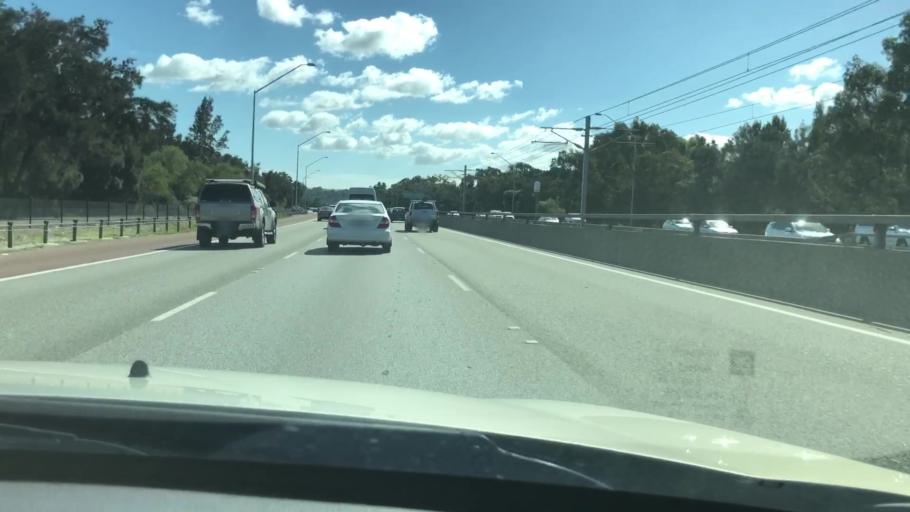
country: AU
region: Western Australia
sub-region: South Perth
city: Como
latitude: -31.9852
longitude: 115.8518
